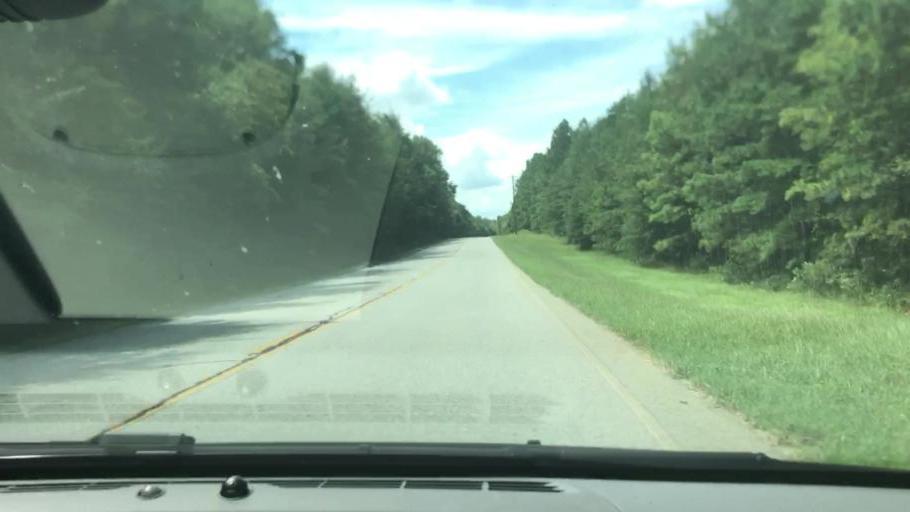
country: US
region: Georgia
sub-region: Stewart County
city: Lumpkin
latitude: 32.1394
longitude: -84.9403
